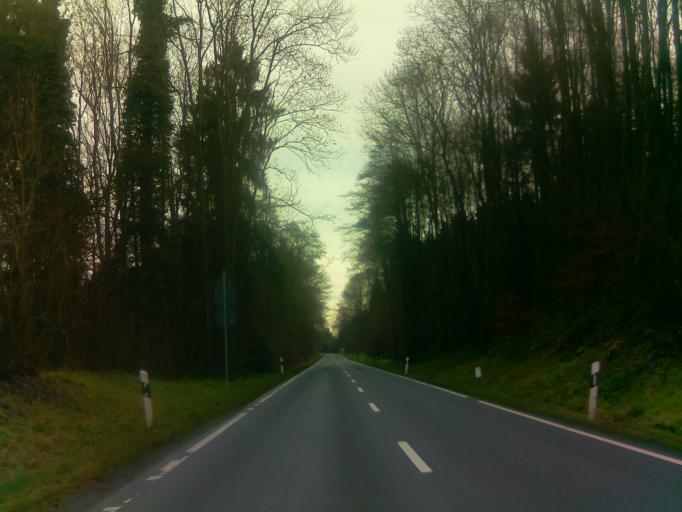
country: DE
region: Hesse
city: Reichelsheim
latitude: 49.6609
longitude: 8.8566
